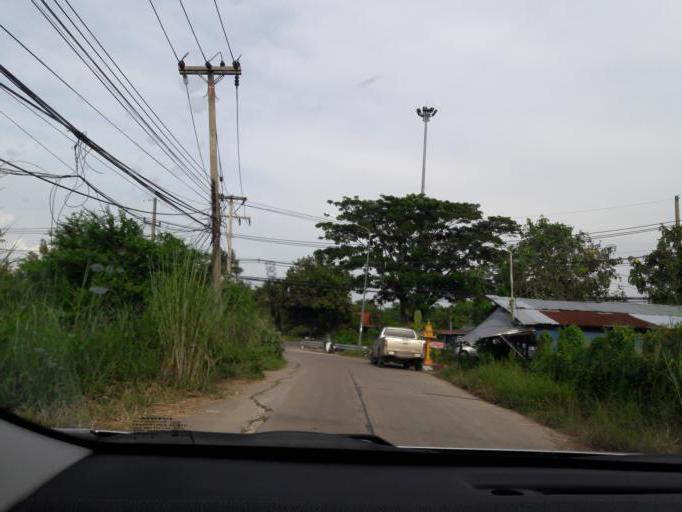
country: TH
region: Ang Thong
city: Ang Thong
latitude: 14.5783
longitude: 100.4528
